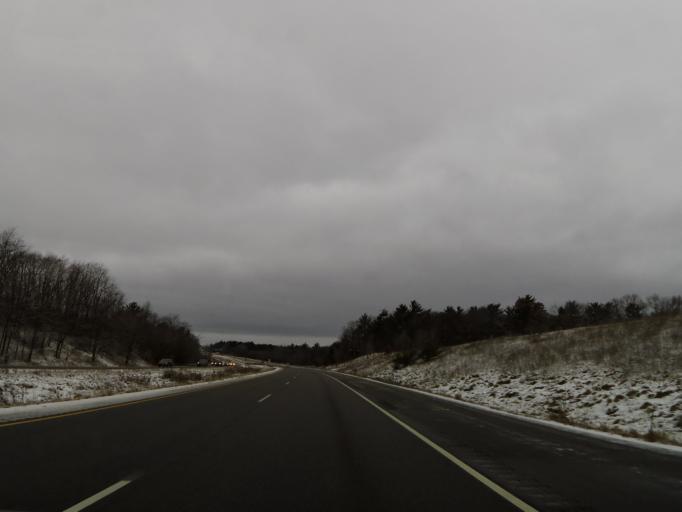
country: US
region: Wisconsin
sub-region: Eau Claire County
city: Altoona
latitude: 44.7642
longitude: -91.4054
